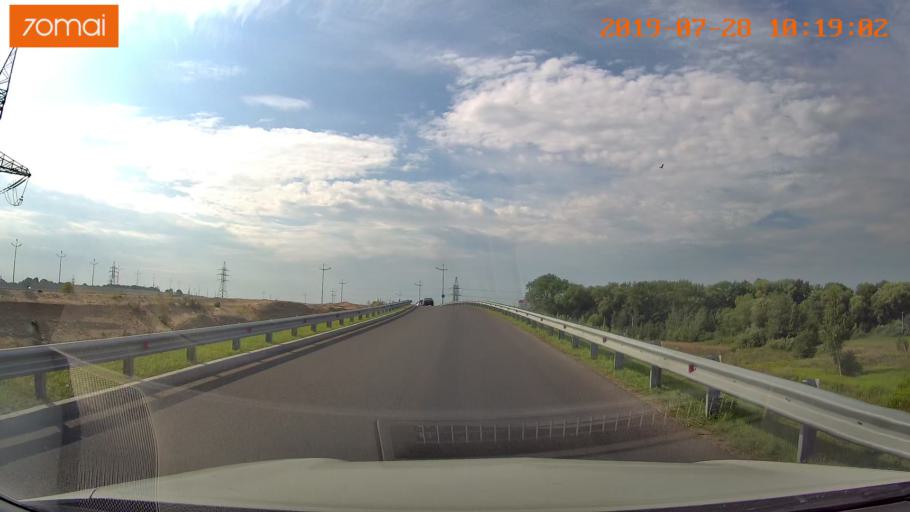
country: RU
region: Kaliningrad
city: Maloye Isakovo
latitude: 54.7512
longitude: 20.5873
